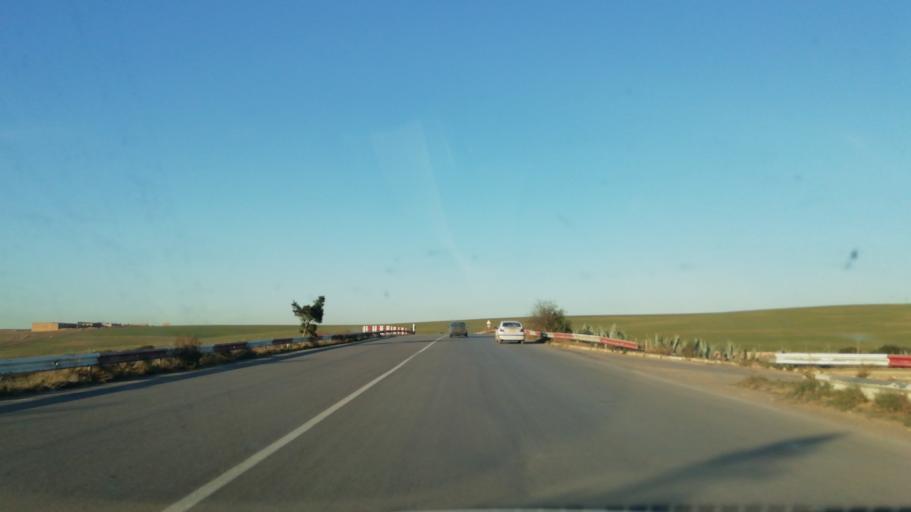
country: DZ
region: Oran
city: Sidi ech Chahmi
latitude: 35.5738
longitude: -0.5563
